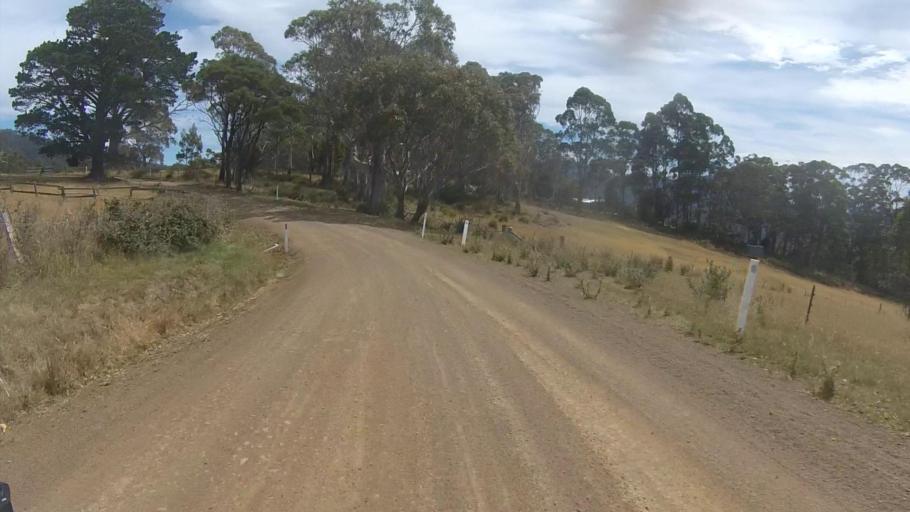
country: AU
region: Tasmania
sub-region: Sorell
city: Sorell
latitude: -42.7815
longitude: 147.8436
